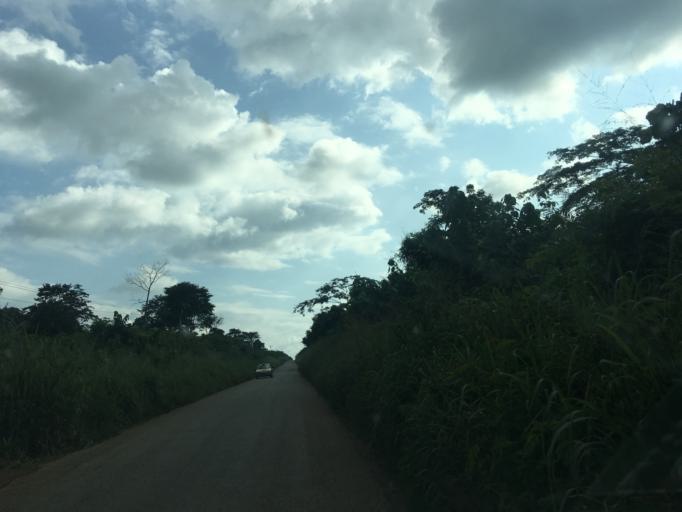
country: GH
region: Western
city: Bibiani
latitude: 6.7812
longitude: -2.5518
